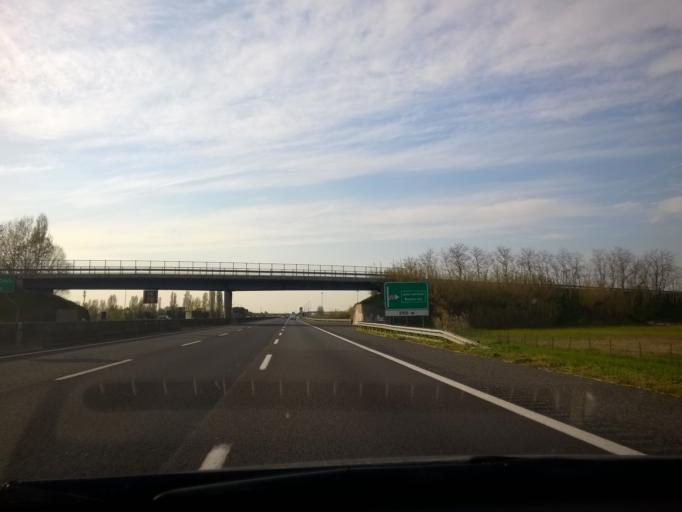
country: IT
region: Emilia-Romagna
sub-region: Forli-Cesena
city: Santa Maria Nuova
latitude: 44.2147
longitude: 12.1814
